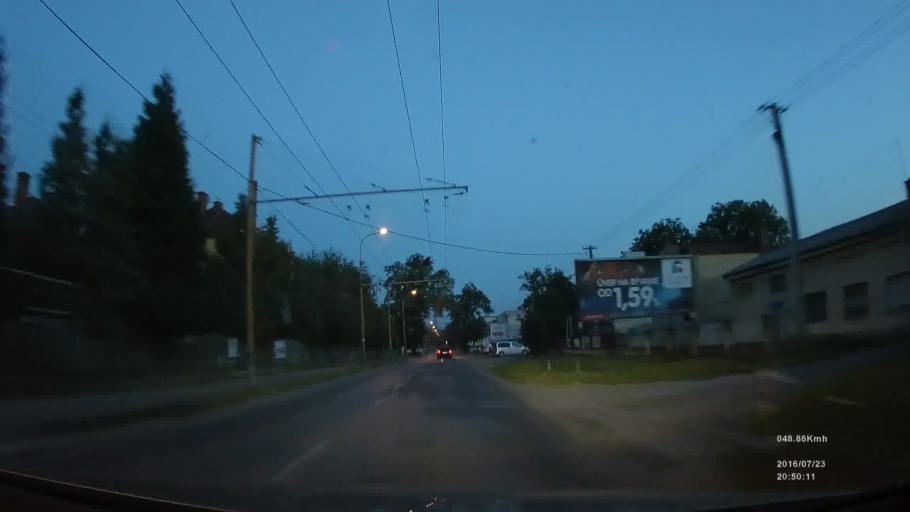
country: SK
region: Presovsky
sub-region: Okres Presov
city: Presov
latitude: 48.9817
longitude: 21.2437
